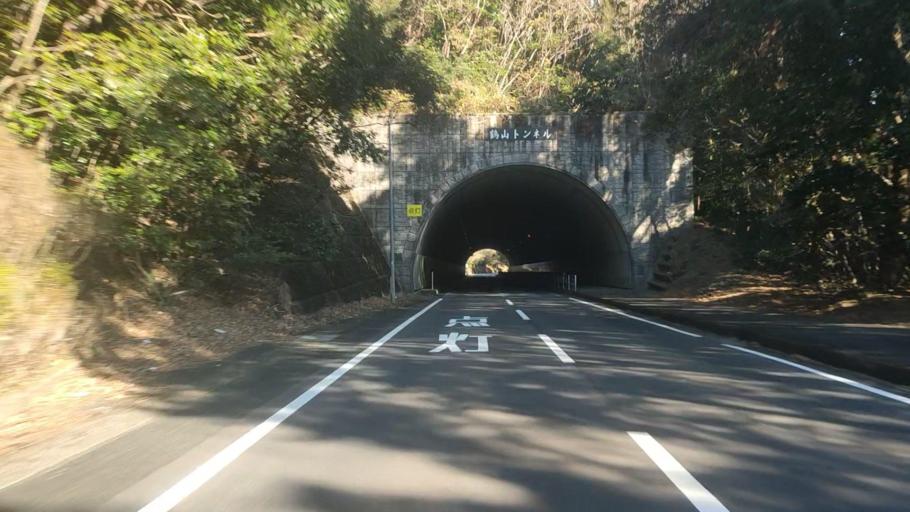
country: JP
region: Miyazaki
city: Nobeoka
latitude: 32.7015
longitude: 131.8153
